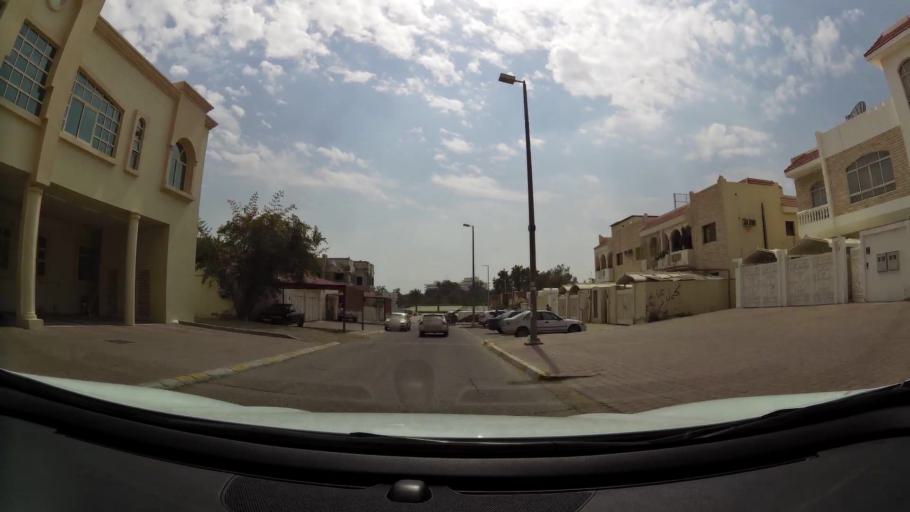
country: AE
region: Abu Dhabi
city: Al Ain
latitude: 24.2121
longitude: 55.7828
